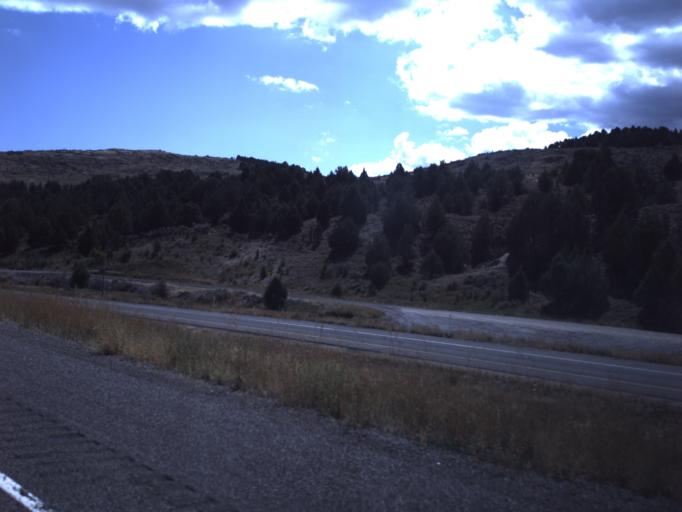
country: US
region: Utah
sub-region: Sevier County
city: Salina
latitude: 38.8792
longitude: -111.5668
